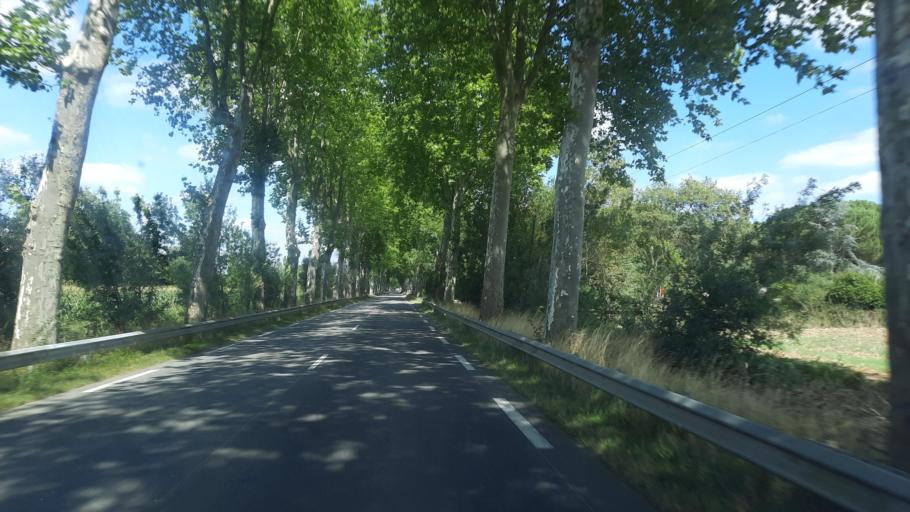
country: FR
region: Midi-Pyrenees
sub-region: Departement du Gers
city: Lombez
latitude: 43.4791
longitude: 0.9244
